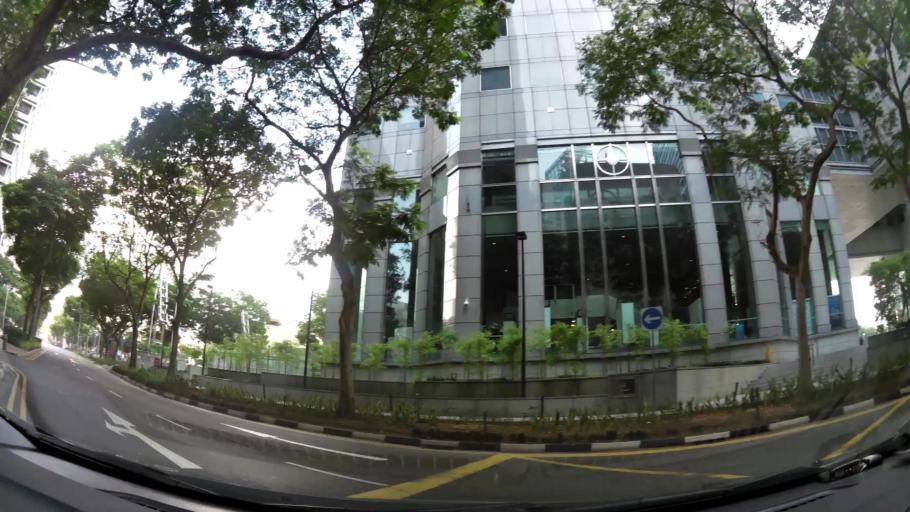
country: SG
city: Singapore
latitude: 1.2847
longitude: 103.8508
